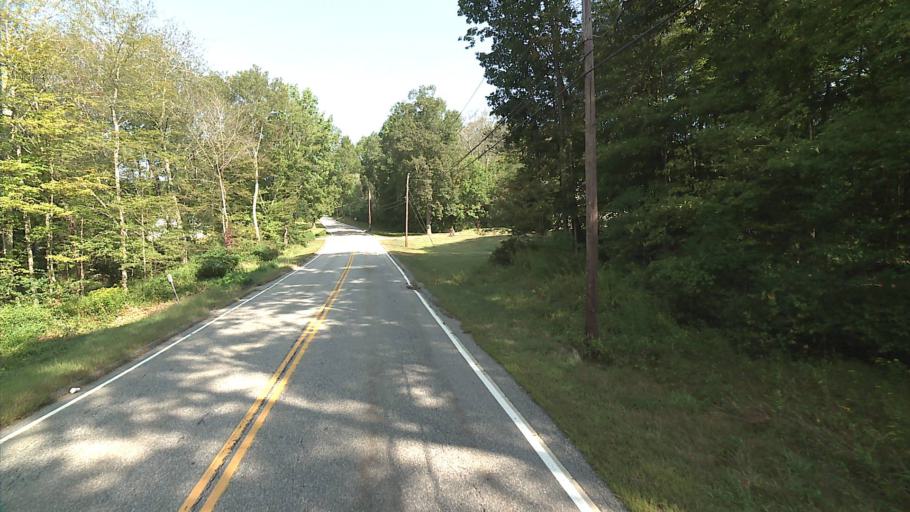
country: US
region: Connecticut
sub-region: Windham County
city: Plainfield Village
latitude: 41.6873
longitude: -71.9677
